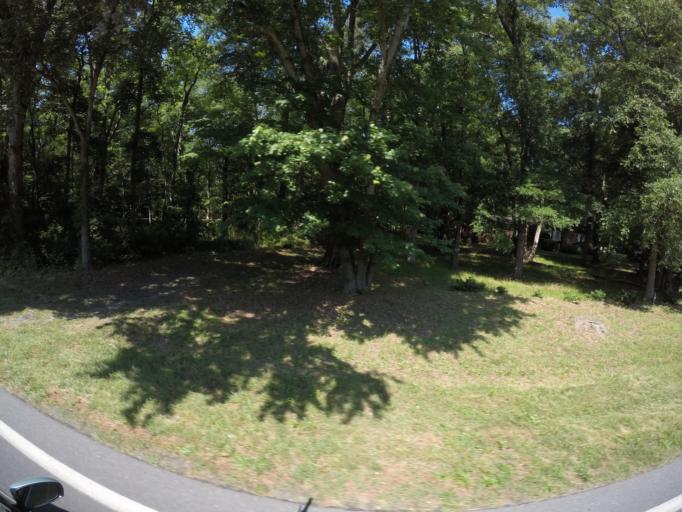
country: US
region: Delaware
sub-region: Sussex County
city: Georgetown
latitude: 38.6901
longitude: -75.3455
